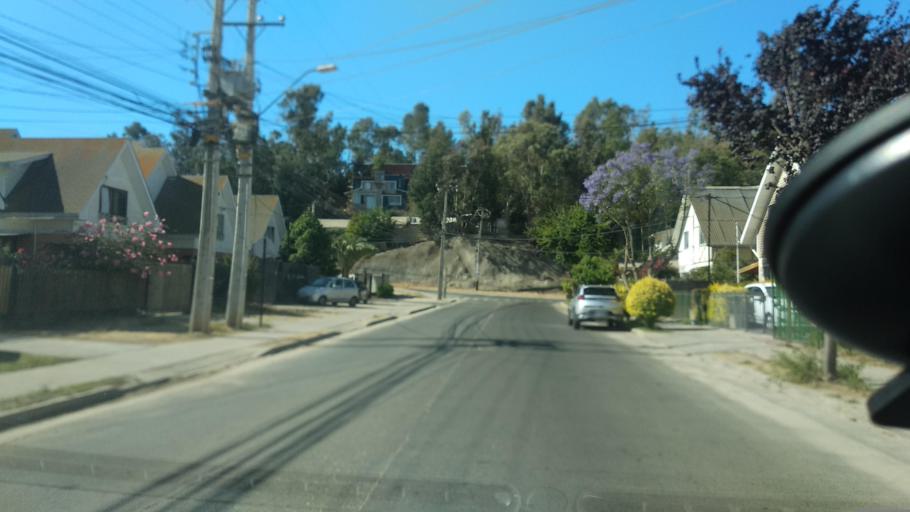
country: CL
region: Valparaiso
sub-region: Provincia de Marga Marga
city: Villa Alemana
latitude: -33.0395
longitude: -71.3903
